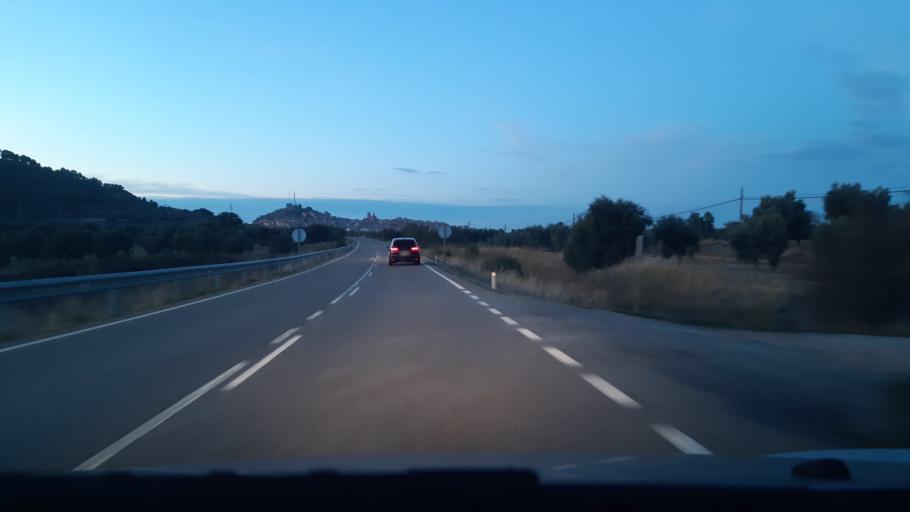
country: ES
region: Aragon
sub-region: Provincia de Teruel
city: Calaceite
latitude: 41.0035
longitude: 0.1930
